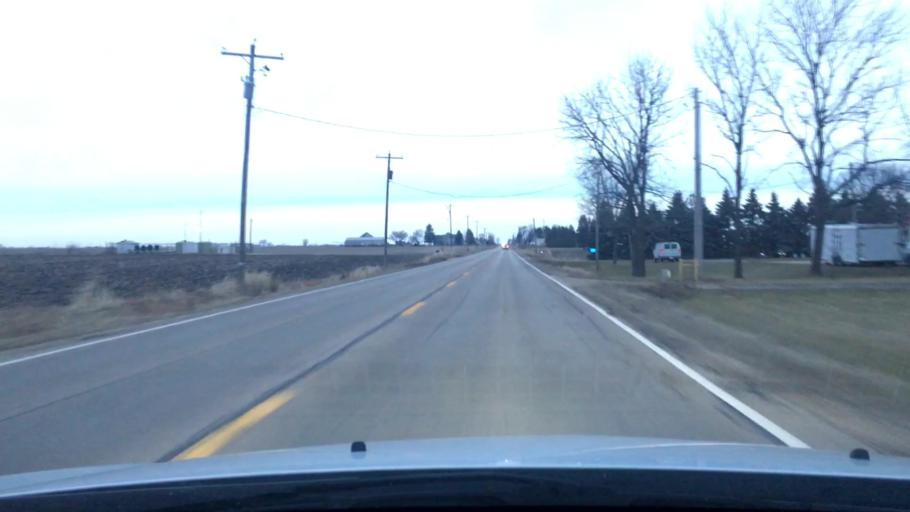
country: US
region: Illinois
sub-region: LaSalle County
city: Peru
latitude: 41.3877
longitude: -89.1258
